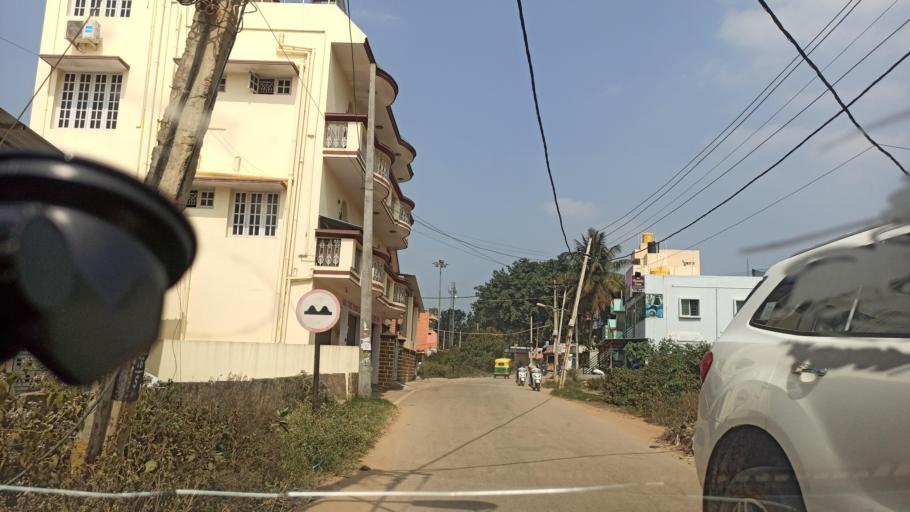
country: IN
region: Karnataka
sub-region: Bangalore Urban
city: Yelahanka
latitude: 13.0899
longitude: 77.6193
